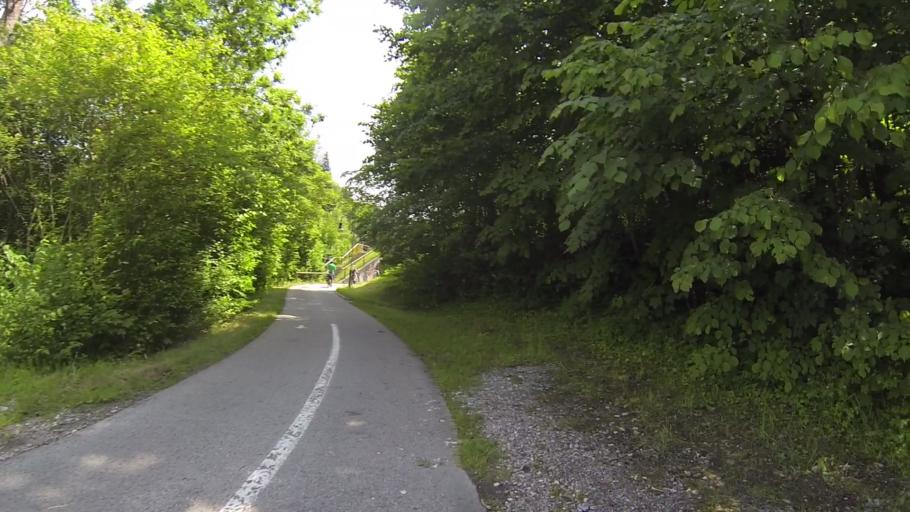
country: DE
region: Bavaria
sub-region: Swabia
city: Fuessen
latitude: 47.5654
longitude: 10.7098
